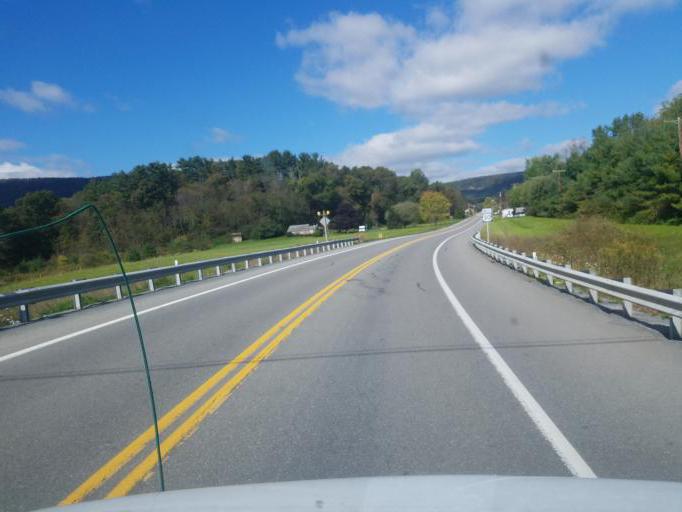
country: US
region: Pennsylvania
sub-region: Fulton County
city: McConnellsburg
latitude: 39.9981
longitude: -78.0978
